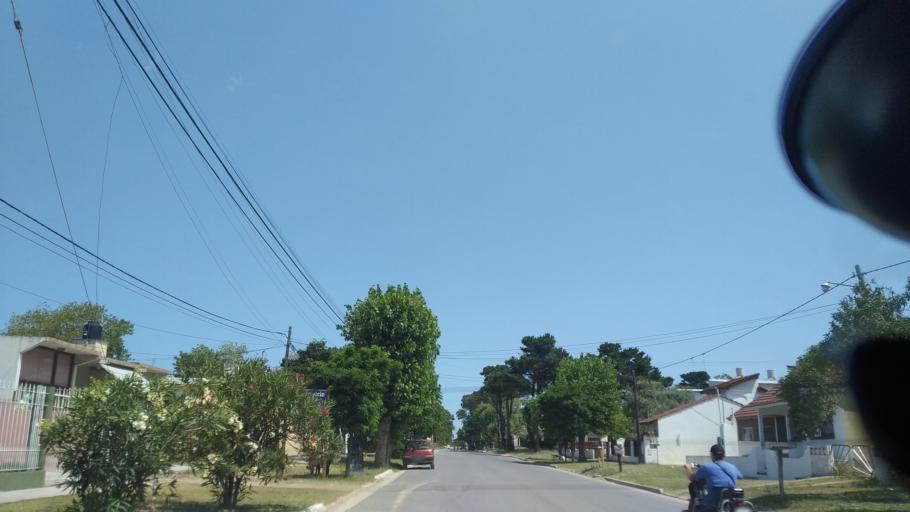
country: AR
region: Buenos Aires
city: Mar del Tuyu
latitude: -36.5755
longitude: -56.6938
